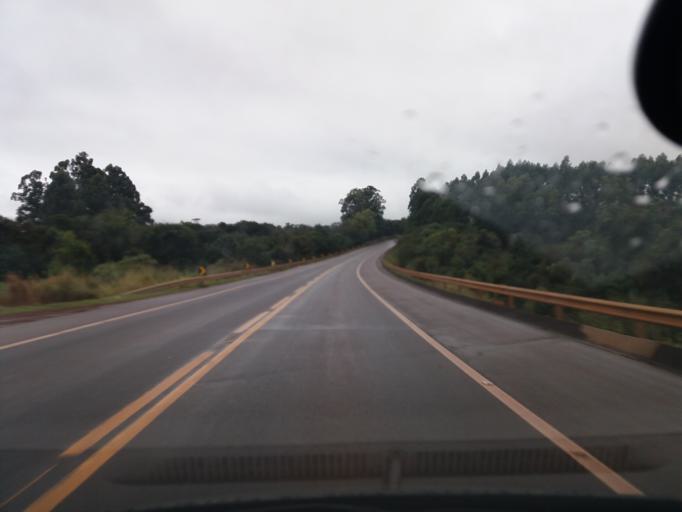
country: BR
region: Parana
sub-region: Campo Mourao
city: Campo Mourao
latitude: -24.3215
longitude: -52.6438
